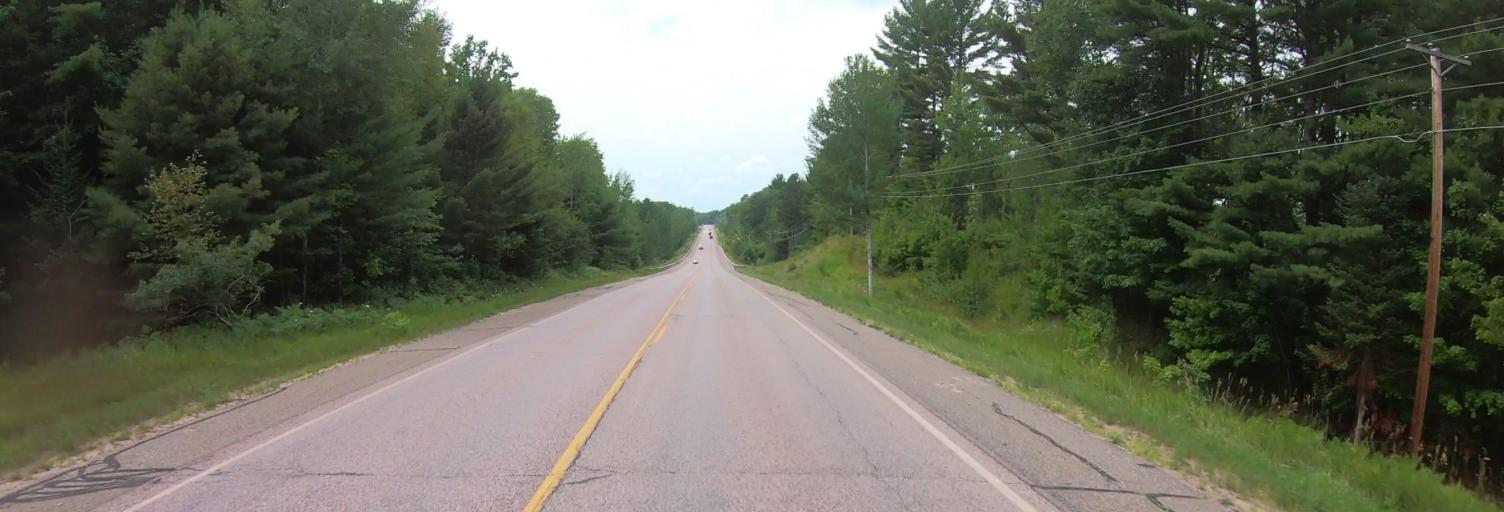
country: US
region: Michigan
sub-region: Marquette County
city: Harvey
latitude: 46.4628
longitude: -87.3673
